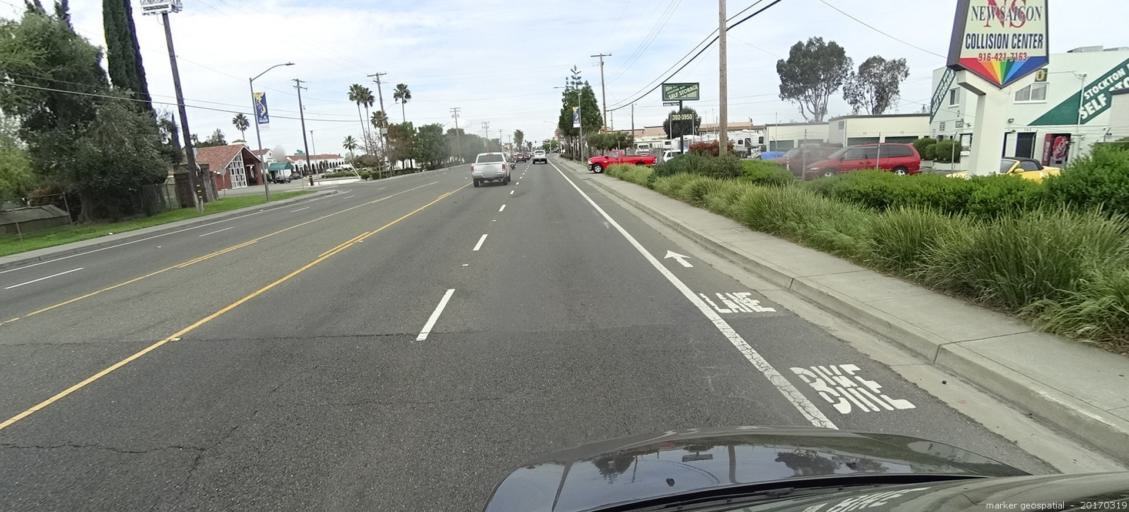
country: US
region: California
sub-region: Sacramento County
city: Parkway
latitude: 38.5133
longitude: -121.4371
